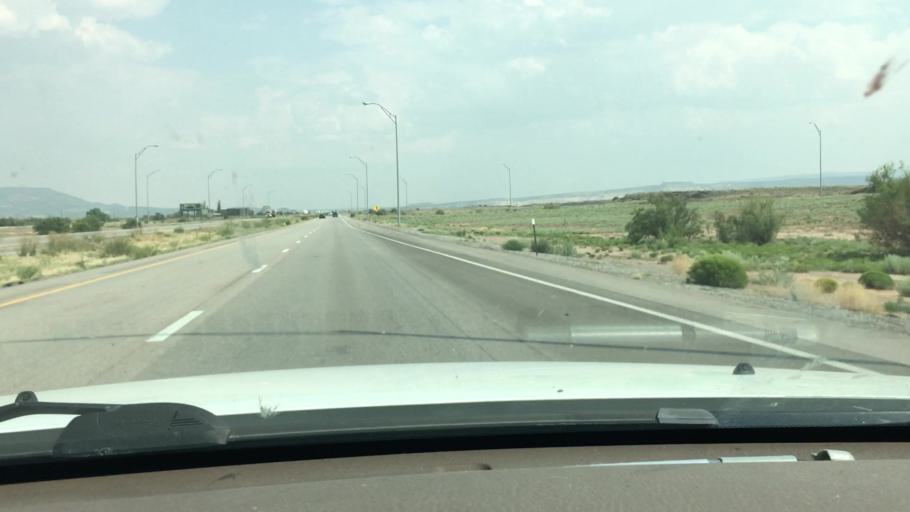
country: US
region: New Mexico
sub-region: Cibola County
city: Grants
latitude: 35.1234
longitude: -107.8289
